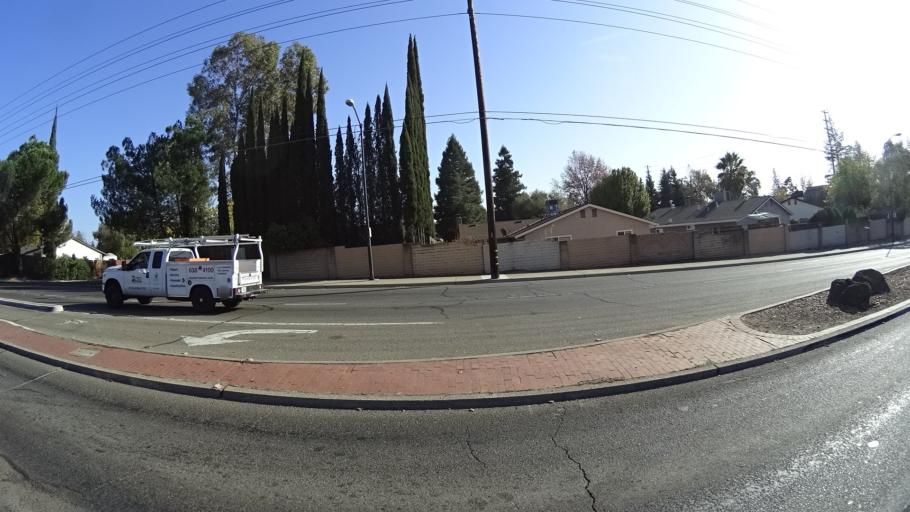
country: US
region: California
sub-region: Sacramento County
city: Citrus Heights
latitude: 38.6864
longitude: -121.2718
